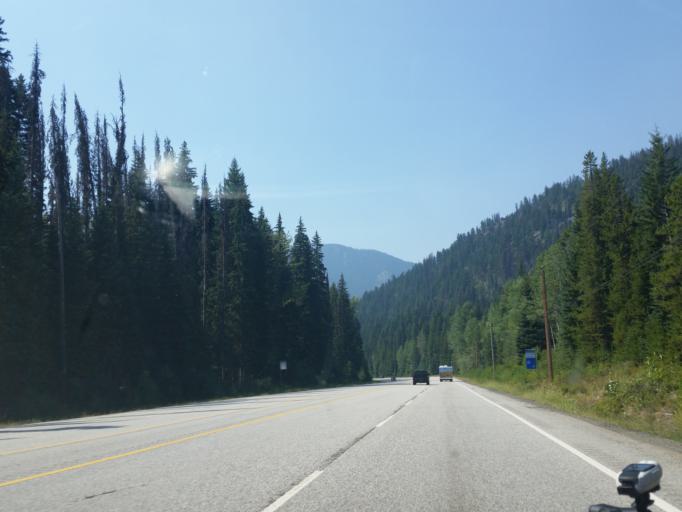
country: CA
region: British Columbia
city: Princeton
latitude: 49.0694
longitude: -120.7197
